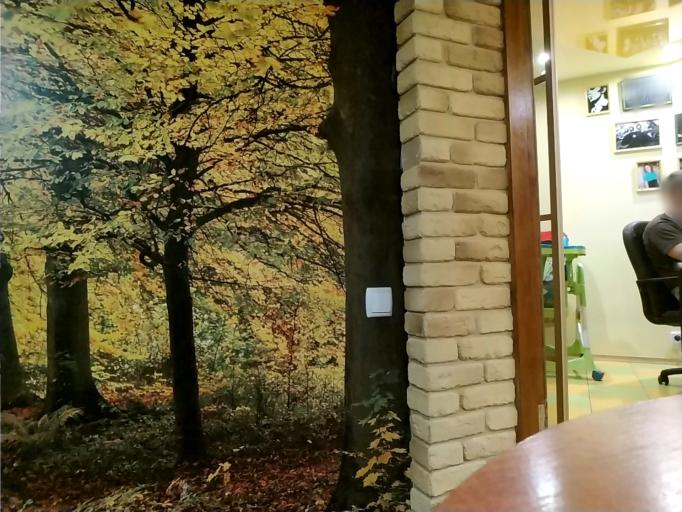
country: RU
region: Tverskaya
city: Zapadnaya Dvina
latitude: 56.3194
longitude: 31.9303
